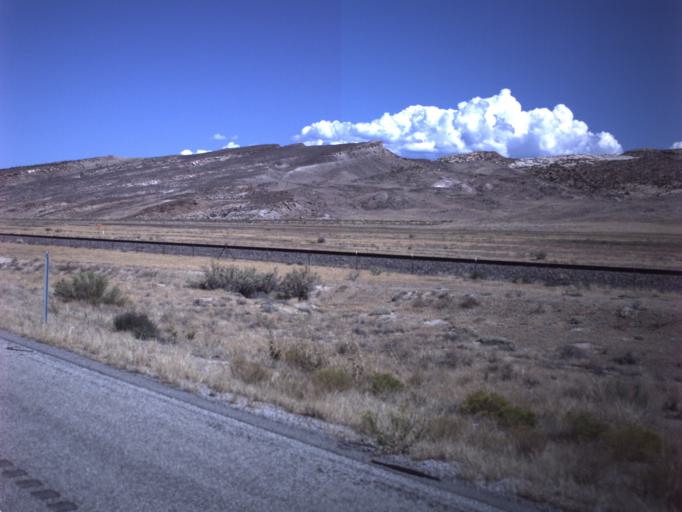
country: US
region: Utah
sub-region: Grand County
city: Moab
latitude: 38.8288
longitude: -109.7845
